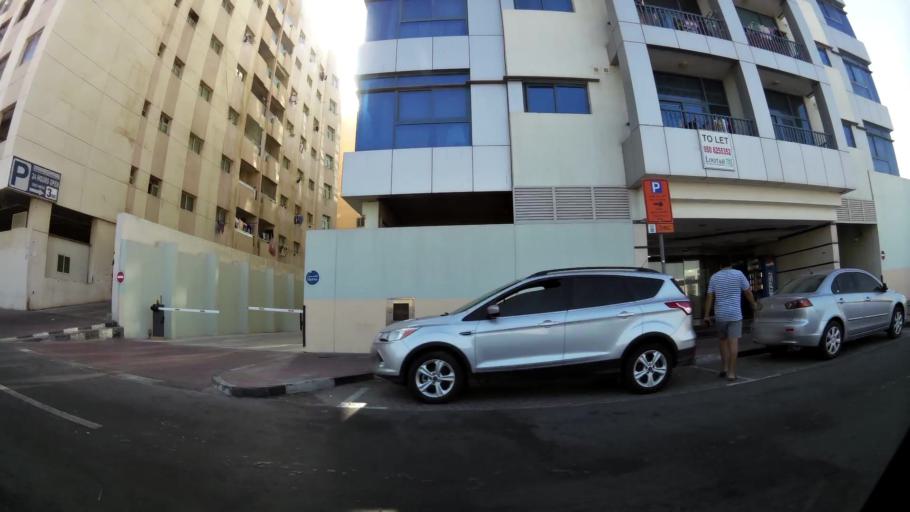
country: AE
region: Ash Shariqah
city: Sharjah
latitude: 25.2547
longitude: 55.2892
